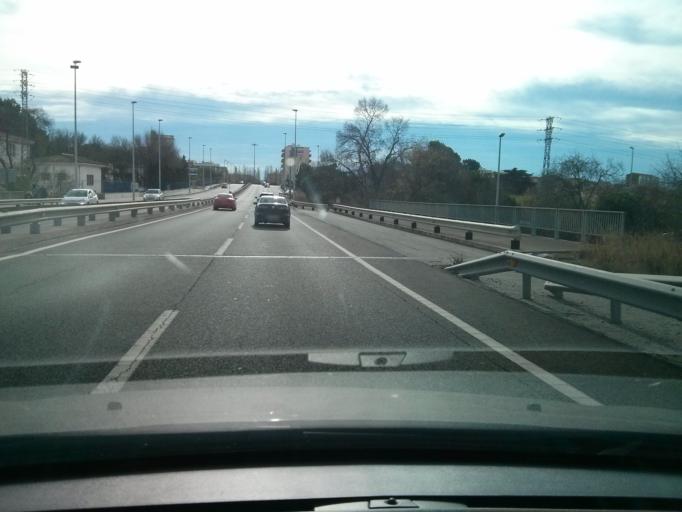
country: ES
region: Catalonia
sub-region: Provincia de Tarragona
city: Tarragona
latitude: 41.1287
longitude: 1.2410
